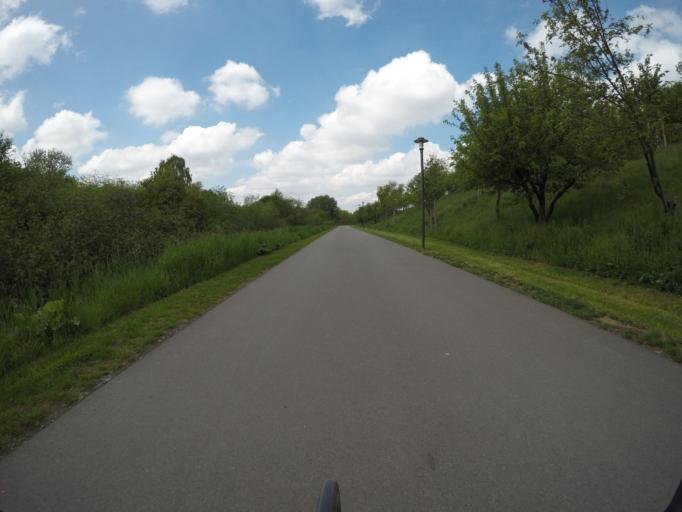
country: DE
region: Berlin
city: Kaulsdorf
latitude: 52.5316
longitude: 13.5801
